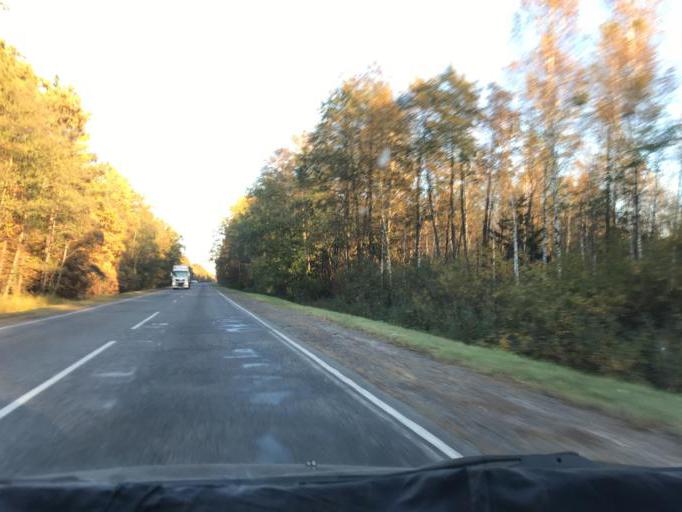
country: BY
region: Gomel
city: Zhytkavichy
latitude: 52.2748
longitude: 28.1740
